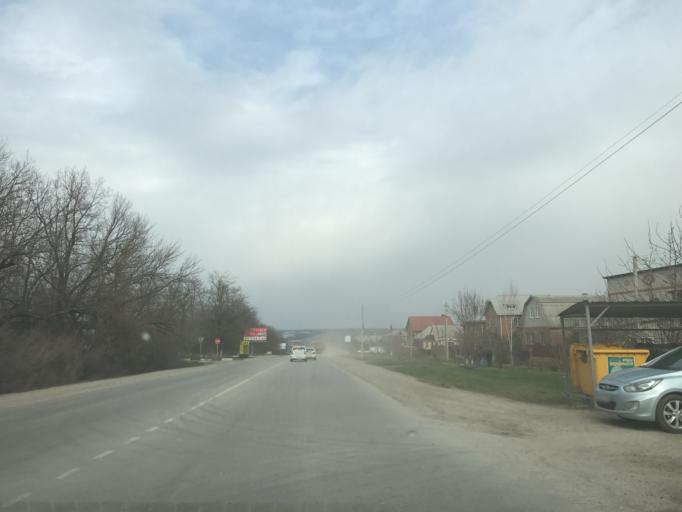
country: RU
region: Rostov
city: Aksay
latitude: 47.2832
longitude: 39.9020
